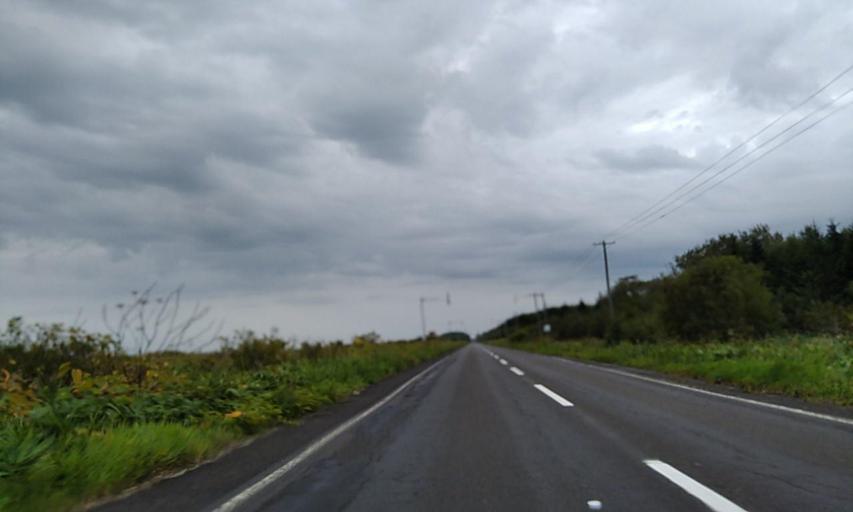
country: JP
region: Hokkaido
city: Nayoro
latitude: 44.6808
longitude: 142.8475
